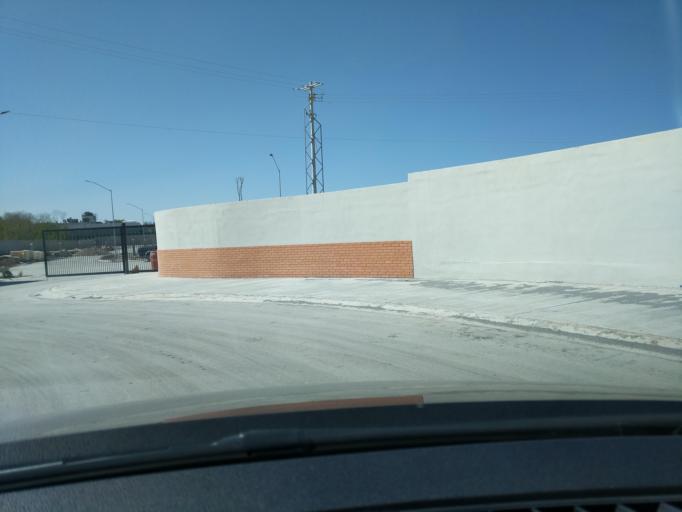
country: MX
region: Nuevo Leon
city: Juarez
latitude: 25.6388
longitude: -100.0823
